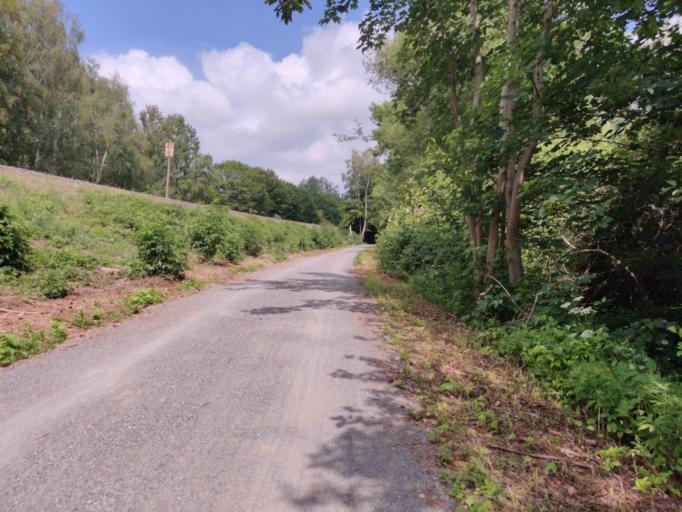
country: DE
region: Lower Saxony
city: Hildesheim
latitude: 52.1249
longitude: 9.9664
